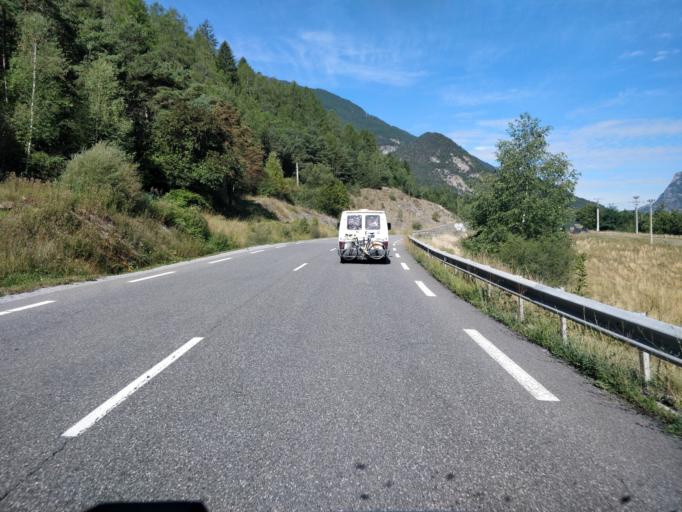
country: FR
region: Provence-Alpes-Cote d'Azur
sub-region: Departement des Alpes-de-Haute-Provence
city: Seyne-les-Alpes
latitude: 44.4014
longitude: 6.4664
